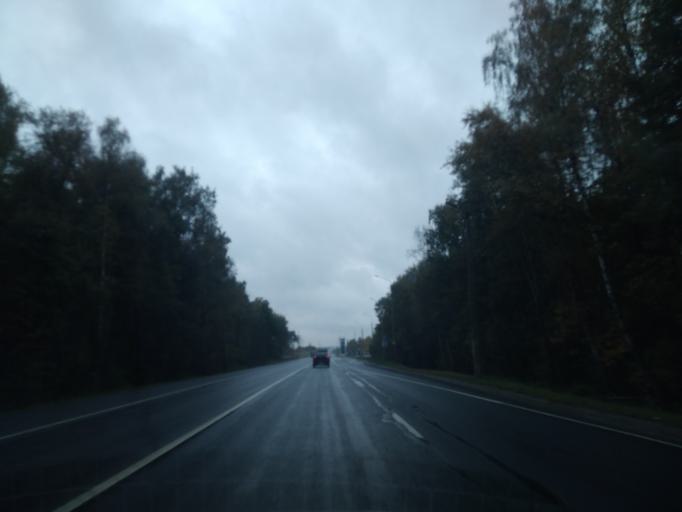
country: RU
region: Tula
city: Barsuki
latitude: 54.2689
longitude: 37.5340
